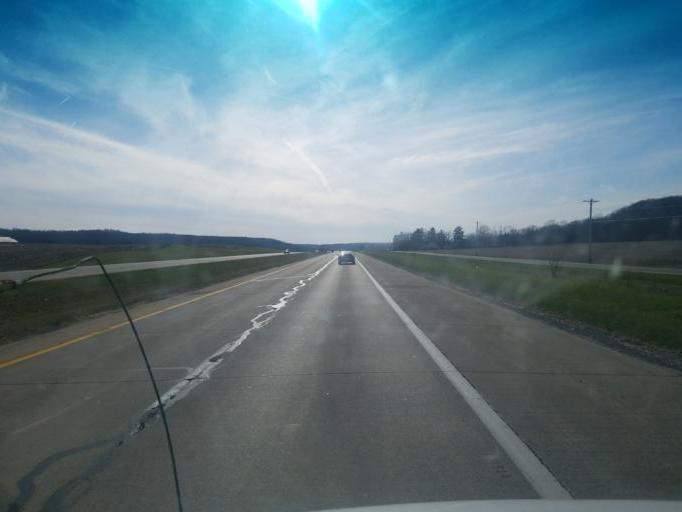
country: US
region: Ohio
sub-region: Champaign County
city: North Lewisburg
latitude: 40.3259
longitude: -83.6351
